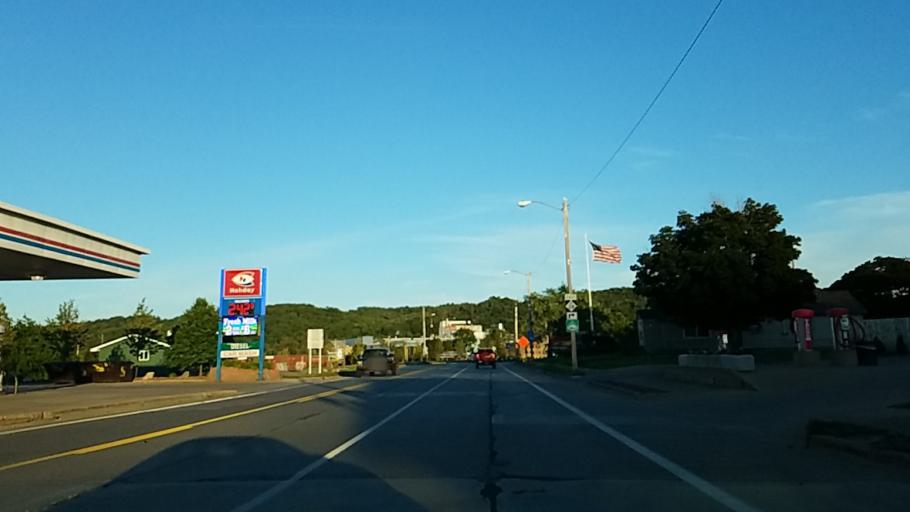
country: US
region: Michigan
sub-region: Alger County
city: Munising
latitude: 46.4103
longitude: -86.6514
